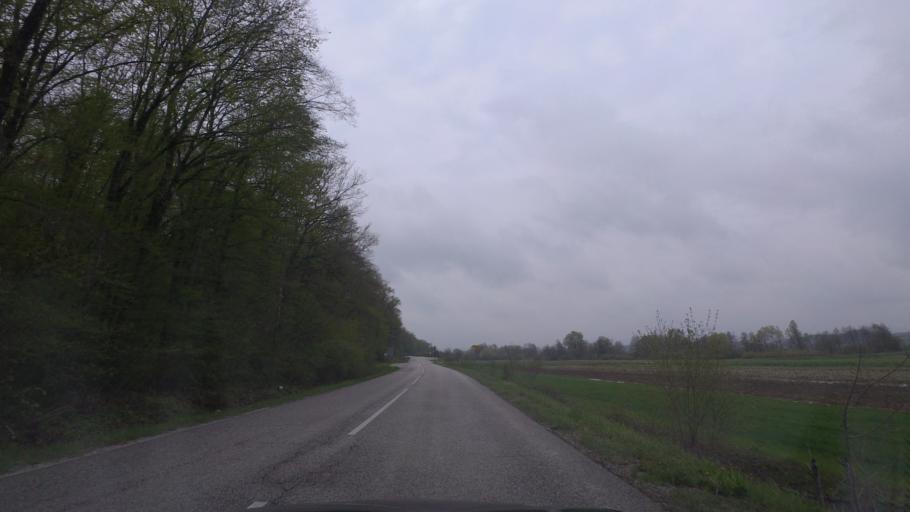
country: HR
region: Karlovacka
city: Ozalj
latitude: 45.6238
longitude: 15.5576
